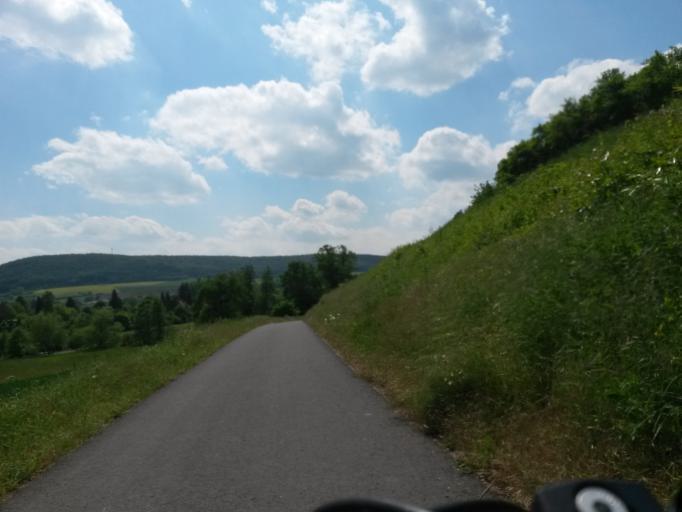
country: DE
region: Bavaria
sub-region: Regierungsbezirk Unterfranken
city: Euerdorf
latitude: 50.1562
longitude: 10.0200
